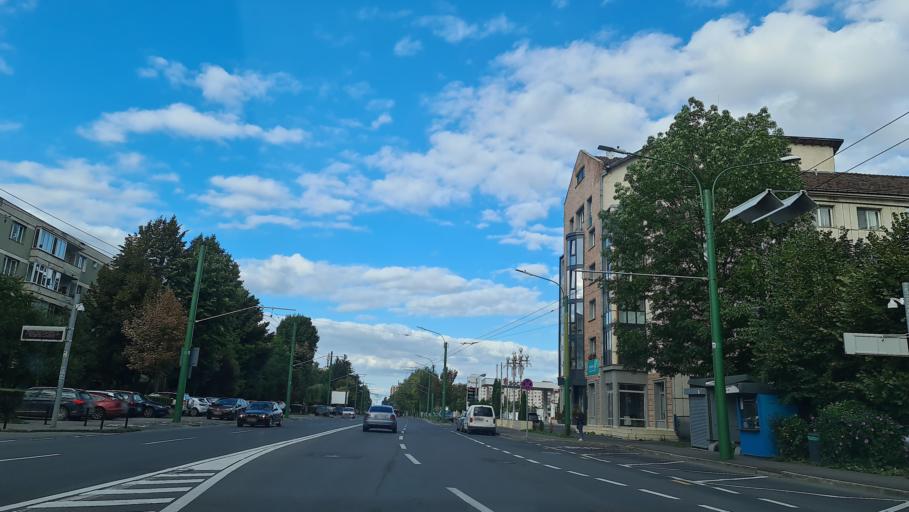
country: RO
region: Brasov
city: Brasov
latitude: 45.6544
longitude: 25.6154
